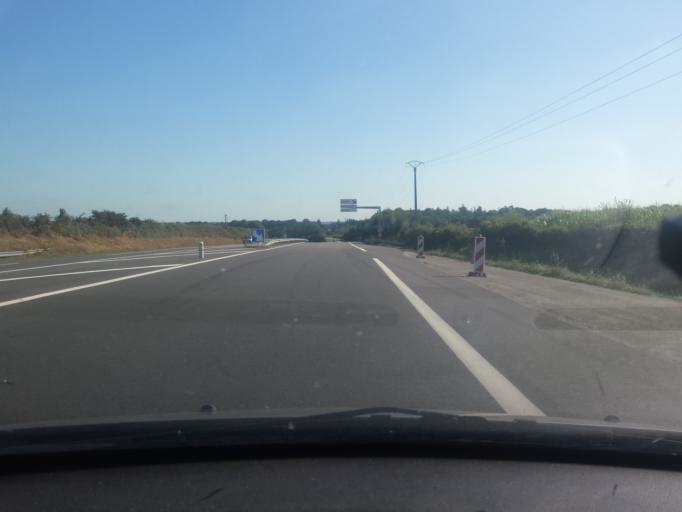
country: FR
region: Brittany
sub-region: Departement du Morbihan
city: Saint-Thuriau
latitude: 48.0099
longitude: -2.9054
